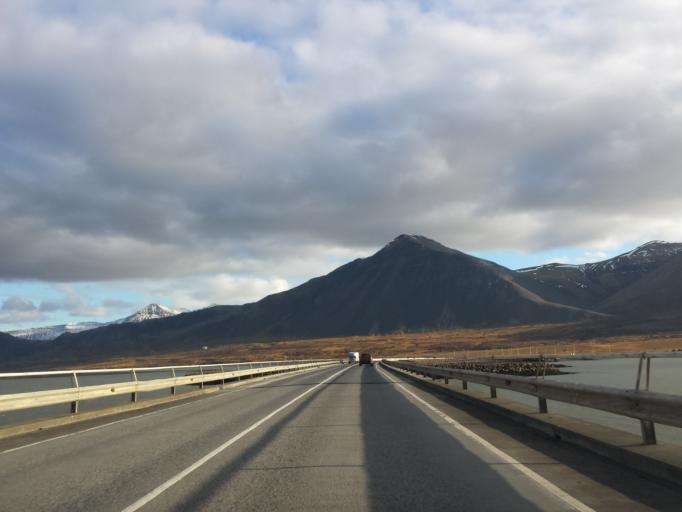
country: IS
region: West
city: Borgarnes
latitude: 64.5337
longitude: -21.8925
